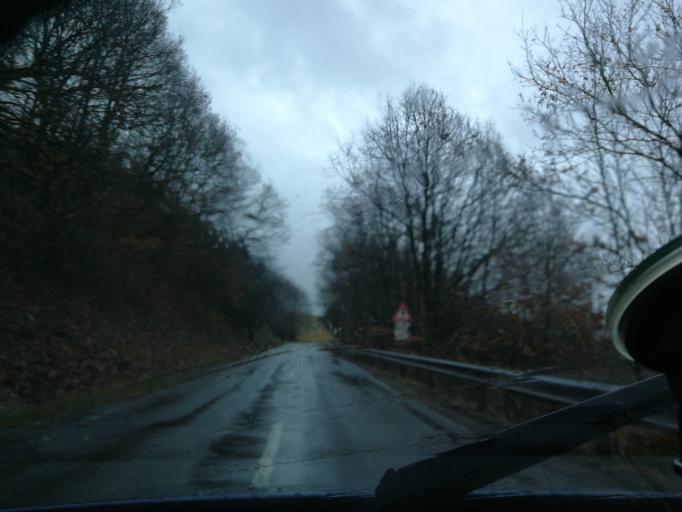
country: DE
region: Rheinland-Pfalz
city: Berglicht
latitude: 49.7945
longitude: 6.9643
